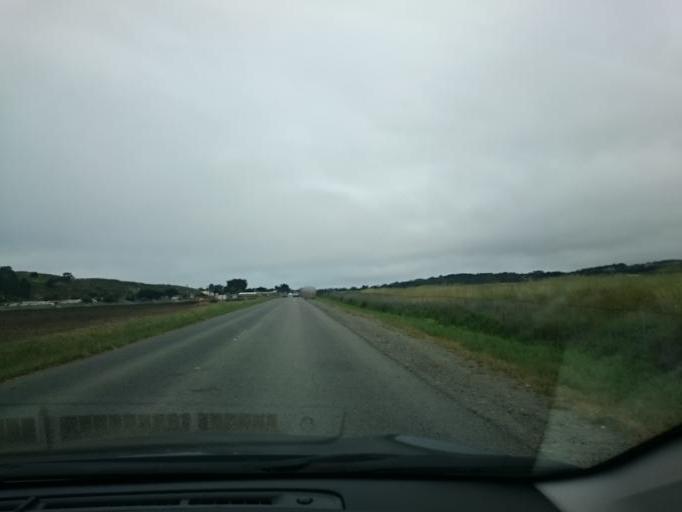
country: US
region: California
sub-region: San Mateo County
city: El Granada
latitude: 37.5066
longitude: -122.4947
